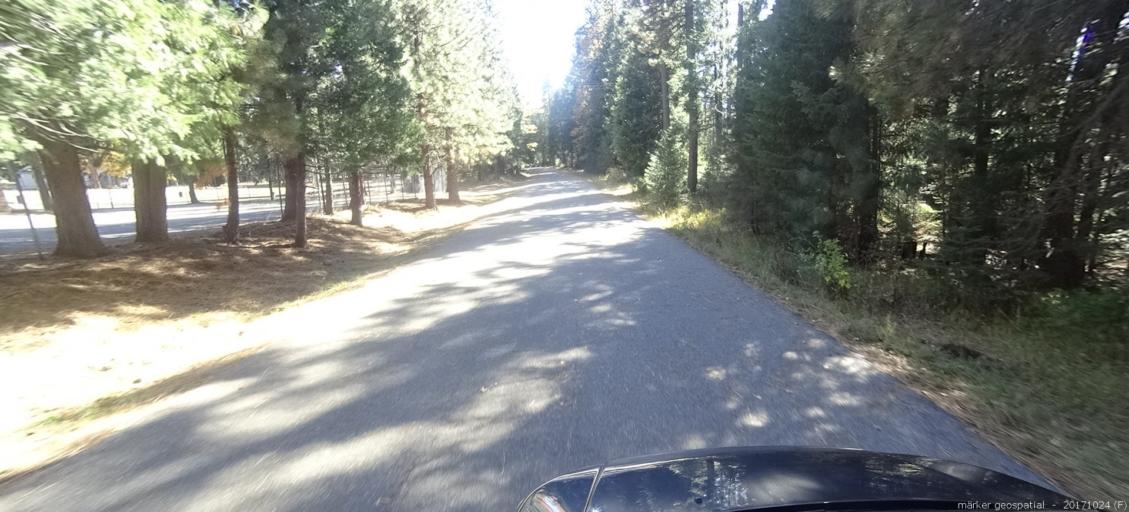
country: US
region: California
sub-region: Shasta County
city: Shingletown
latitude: 40.5183
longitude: -121.6820
